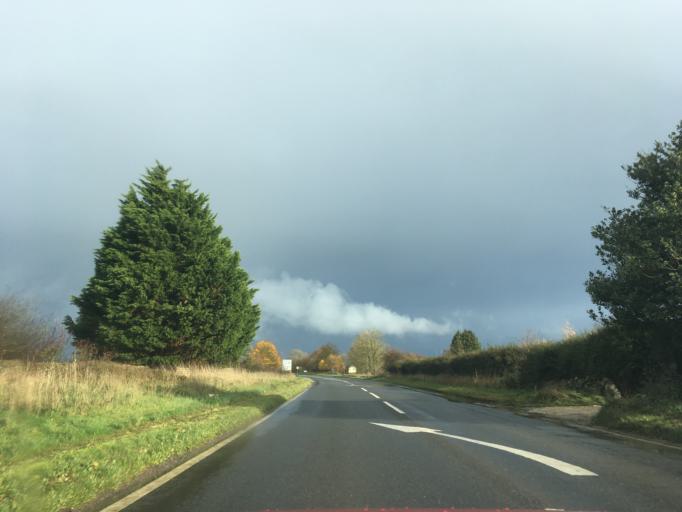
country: GB
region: England
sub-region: South Gloucestershire
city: Marshfield
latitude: 51.4613
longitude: -2.3352
